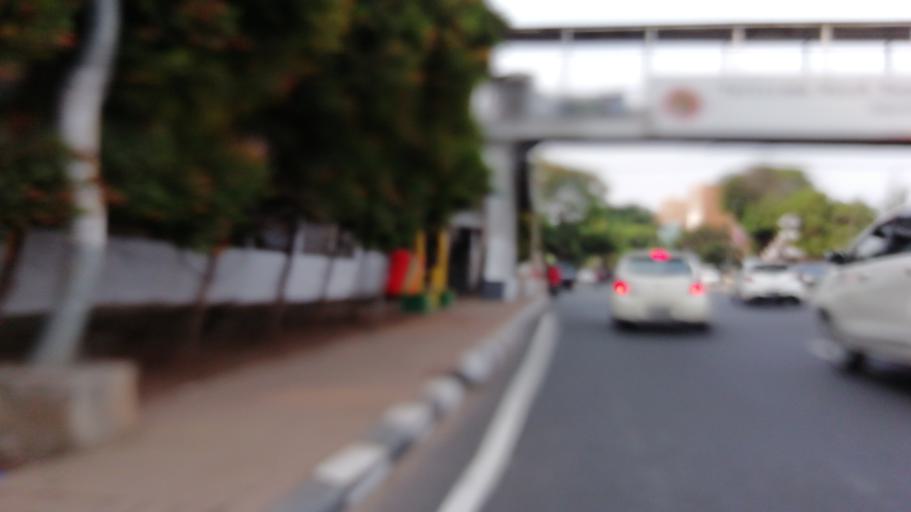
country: ID
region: Jakarta Raya
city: Jakarta
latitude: -6.2888
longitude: 106.8066
